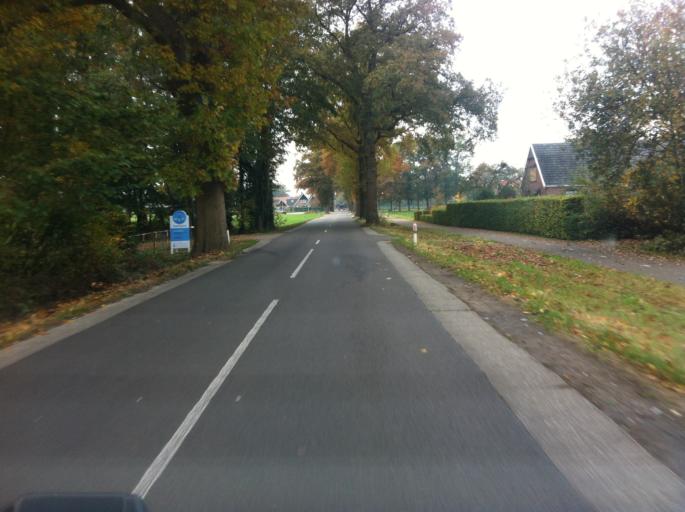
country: NL
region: Gelderland
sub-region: Gemeente Winterswijk
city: Winterswijk
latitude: 51.9775
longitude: 6.7478
